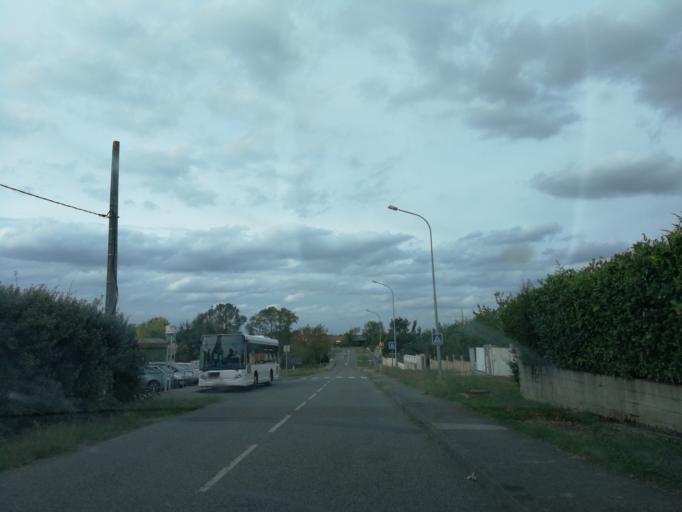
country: FR
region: Midi-Pyrenees
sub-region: Departement de la Haute-Garonne
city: Dremil-Lafage
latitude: 43.6007
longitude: 1.6053
